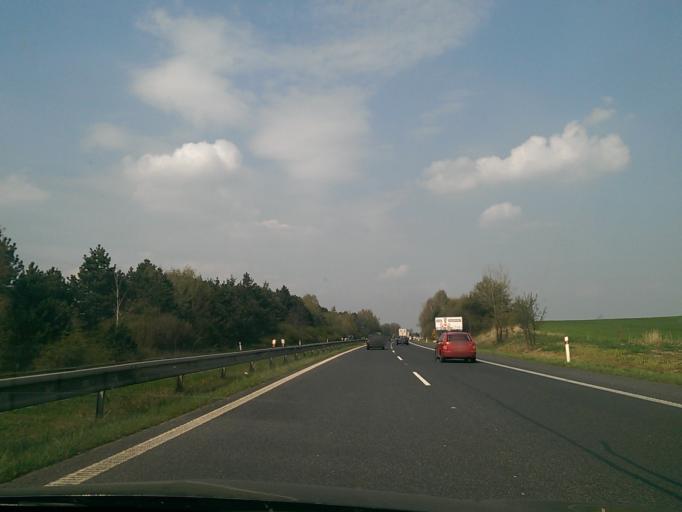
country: CZ
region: Central Bohemia
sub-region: Okres Mlada Boleslav
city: Mlada Boleslav
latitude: 50.3585
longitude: 14.8736
